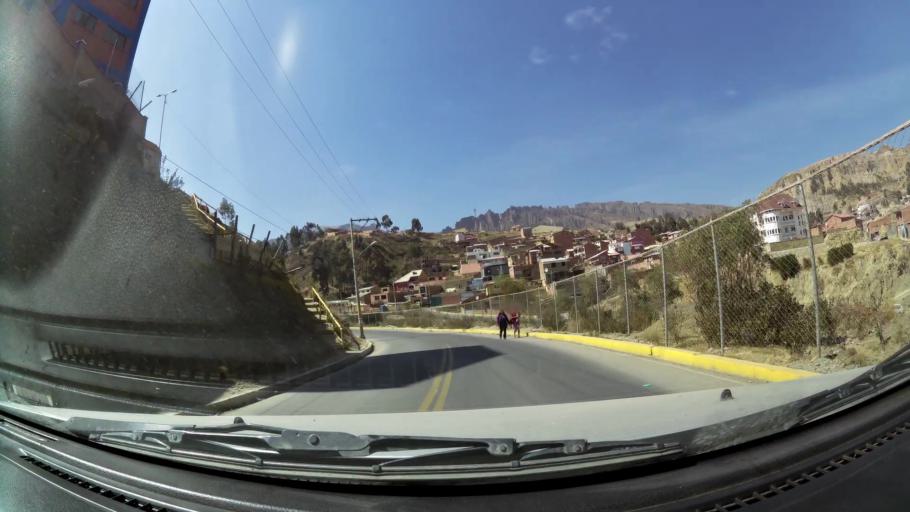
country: BO
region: La Paz
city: La Paz
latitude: -16.5384
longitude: -68.0453
